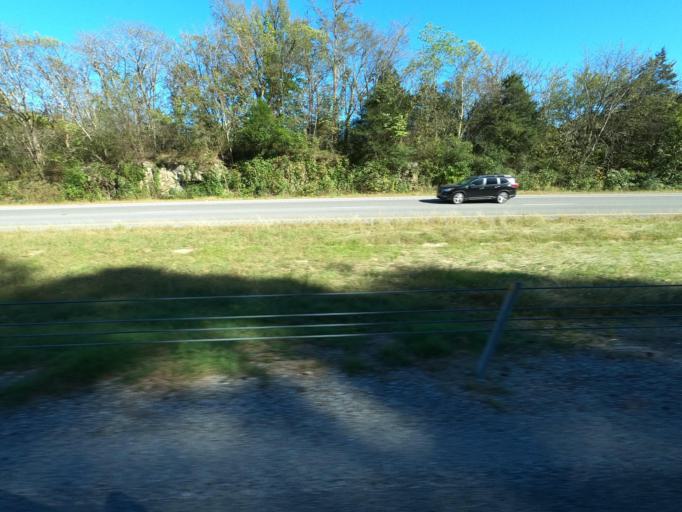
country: US
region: Alabama
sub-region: Limestone County
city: Ardmore
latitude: 34.9982
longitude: -86.8776
